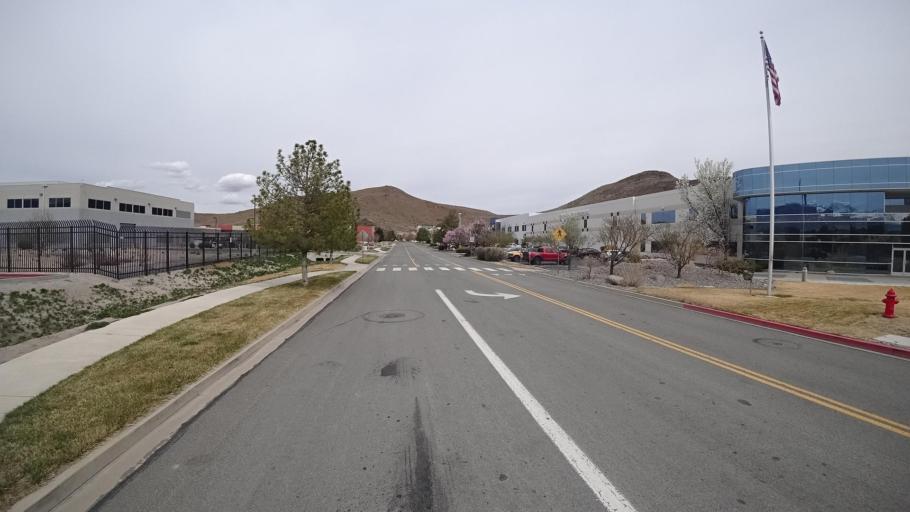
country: US
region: Nevada
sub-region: Washoe County
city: Sparks
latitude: 39.4518
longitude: -119.7542
